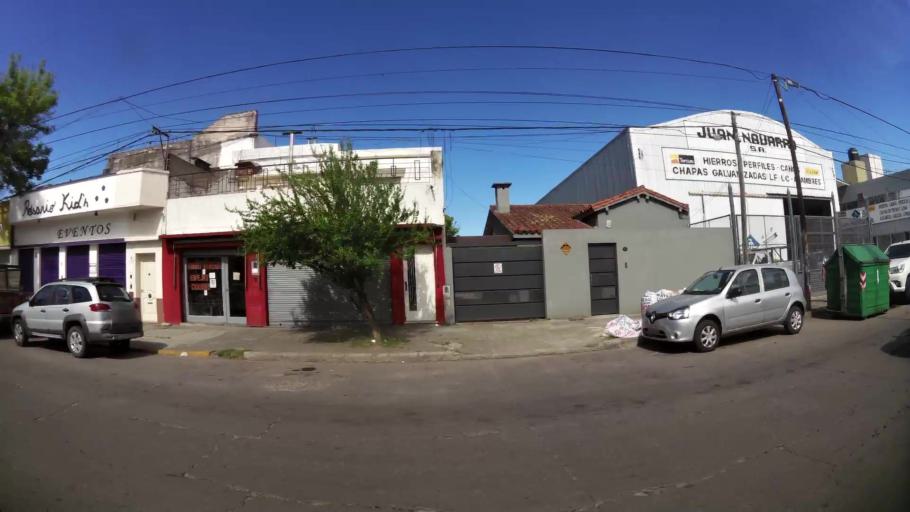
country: AR
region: Santa Fe
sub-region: Departamento de Rosario
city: Rosario
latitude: -32.9337
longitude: -60.7129
